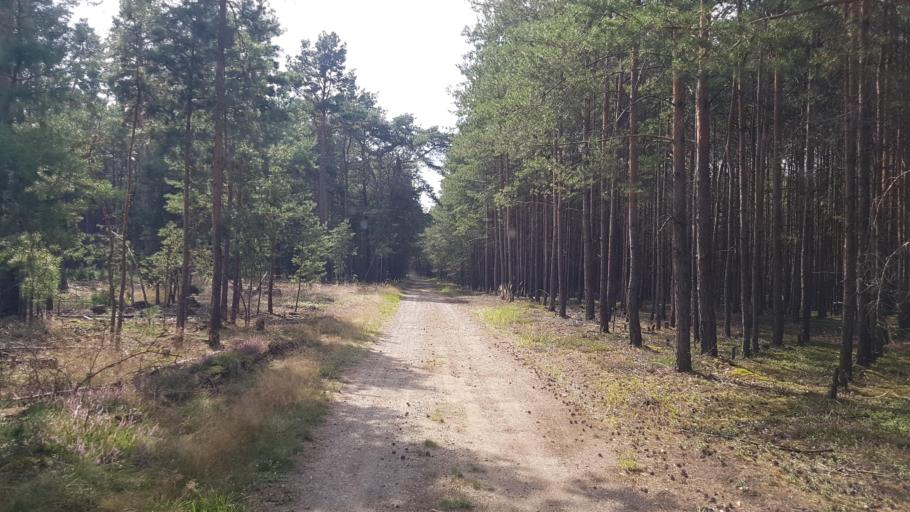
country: DE
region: Brandenburg
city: Schonewalde
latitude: 51.7558
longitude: 13.6041
